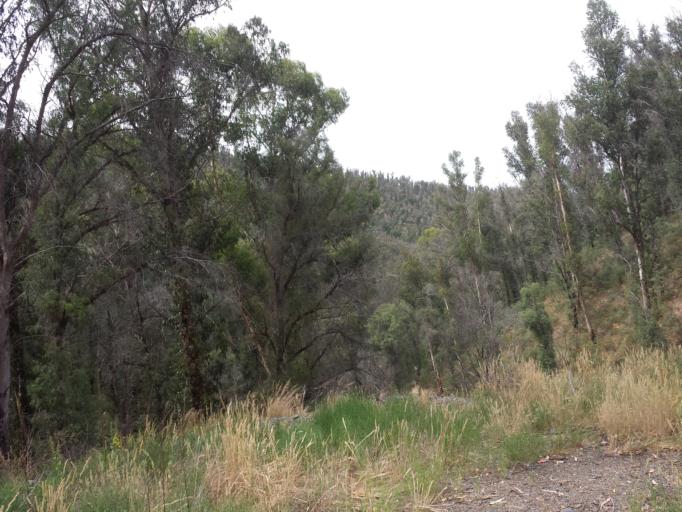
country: AU
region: Victoria
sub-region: Wellington
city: Heyfield
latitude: -37.7343
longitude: 146.4045
